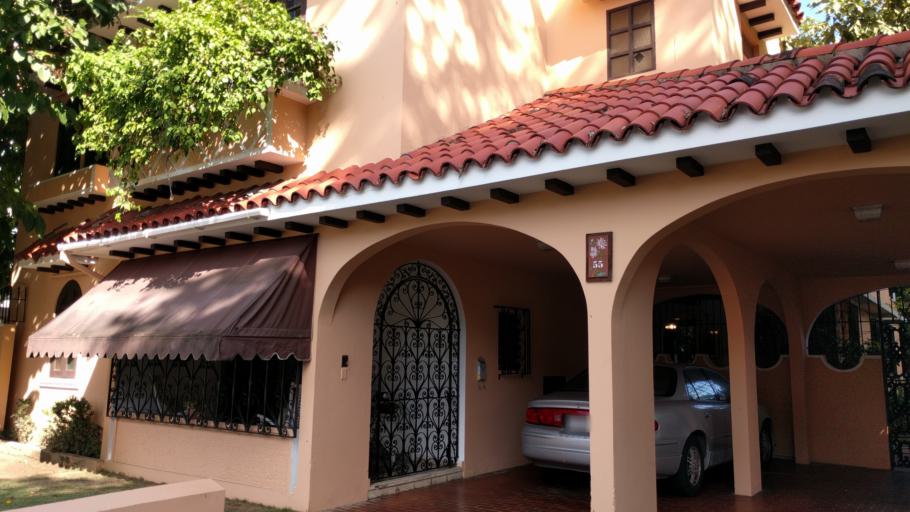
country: PR
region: San Juan
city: San Juan
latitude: 18.4542
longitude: -66.0663
